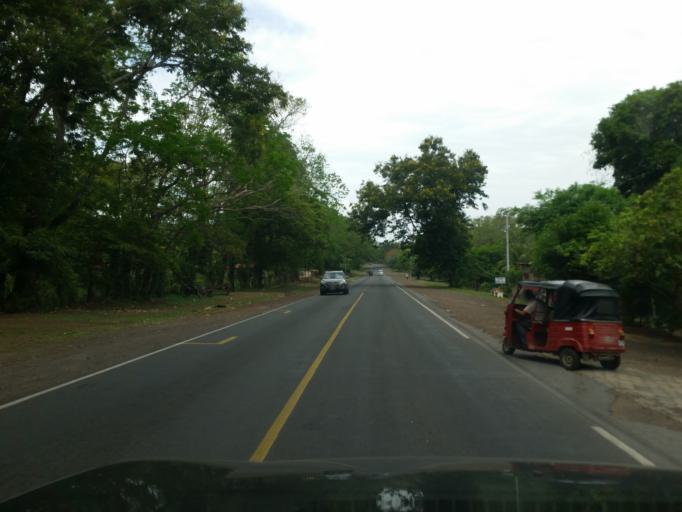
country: NI
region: Granada
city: Diriomo
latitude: 11.8485
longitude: -86.0236
